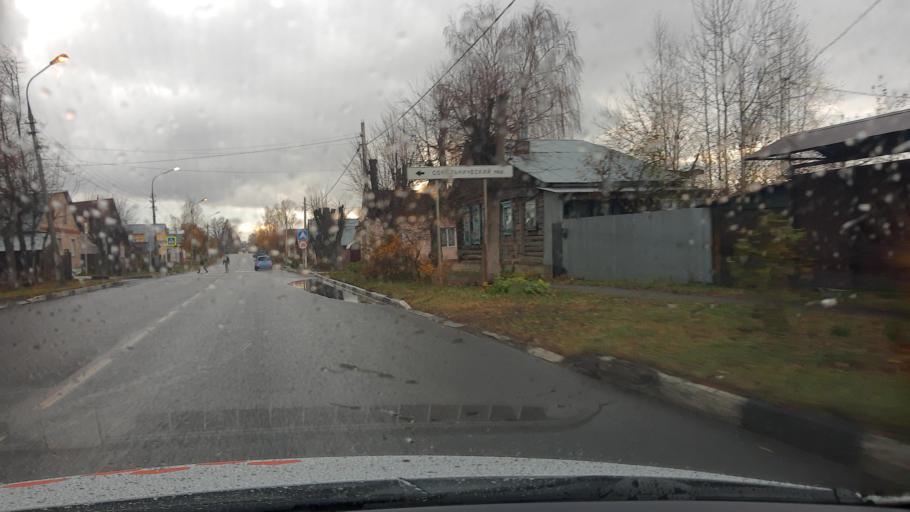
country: RU
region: Moskovskaya
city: Noginsk
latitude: 55.8523
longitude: 38.4244
